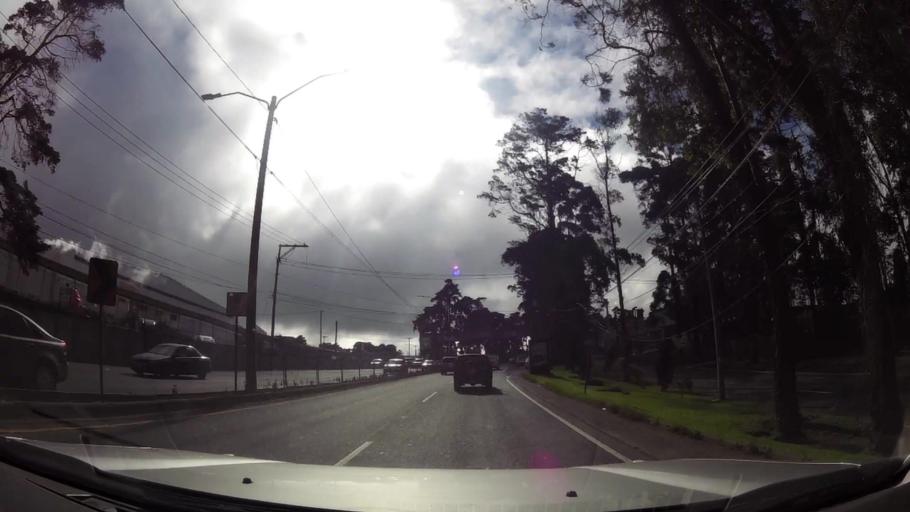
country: GT
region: Guatemala
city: Santa Catarina Pinula
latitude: 14.5566
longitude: -90.4565
